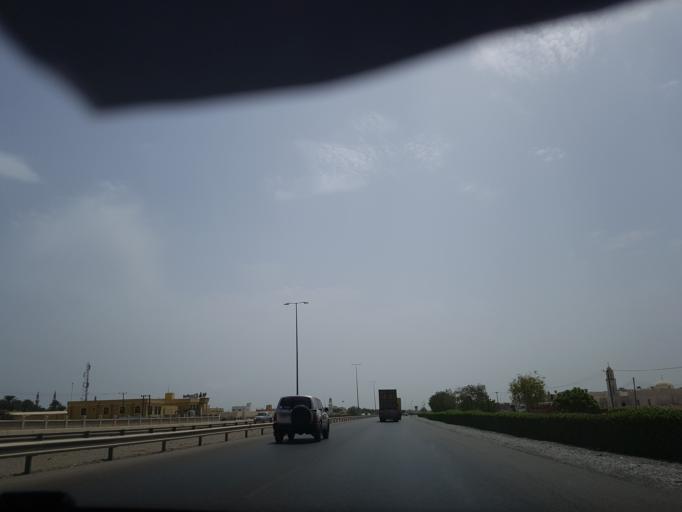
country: OM
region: Al Batinah
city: Barka'
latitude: 23.7354
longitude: 57.6727
